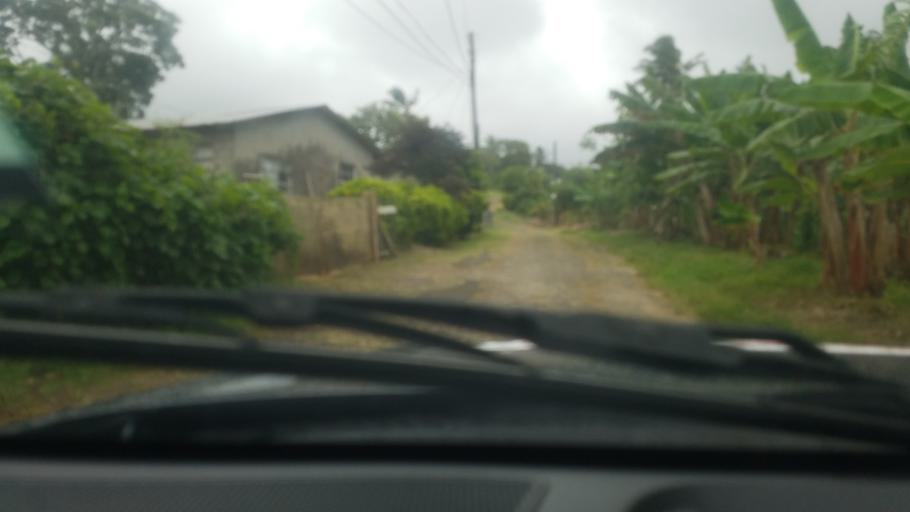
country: LC
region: Micoud Quarter
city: Micoud
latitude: 13.8022
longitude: -60.9455
